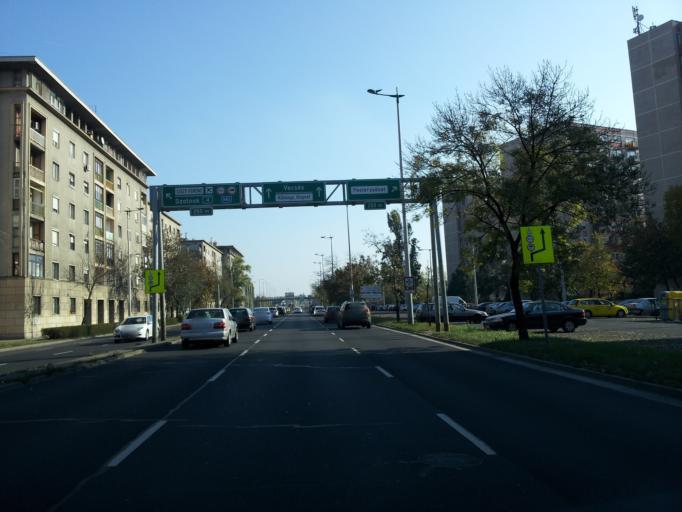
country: HU
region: Budapest
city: Budapest XIX. keruelet
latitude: 47.4679
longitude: 19.1194
